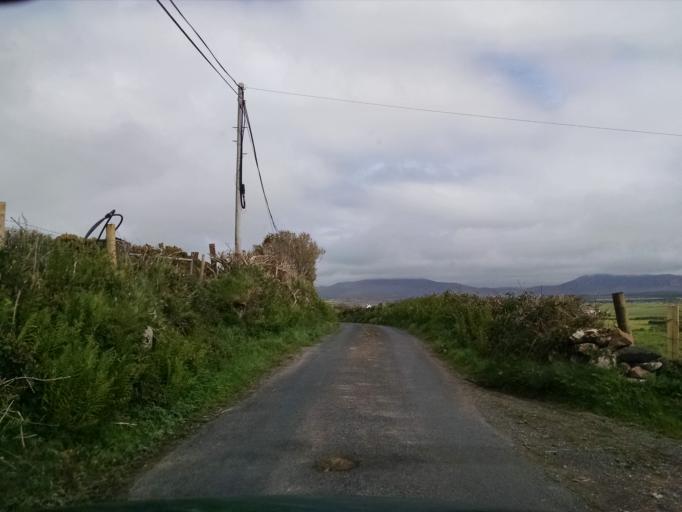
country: IE
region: Connaught
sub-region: County Galway
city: Clifden
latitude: 53.7604
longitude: -9.8475
